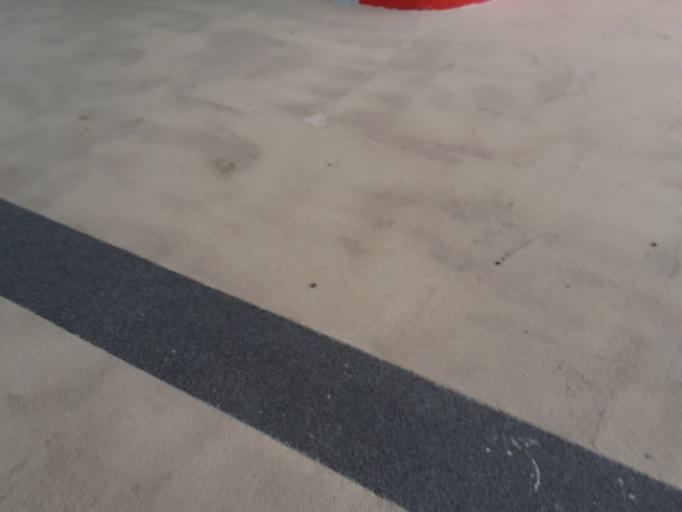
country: IT
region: Sardinia
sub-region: Provincia di Cagliari
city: Monserrato
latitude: 39.2694
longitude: 9.1265
